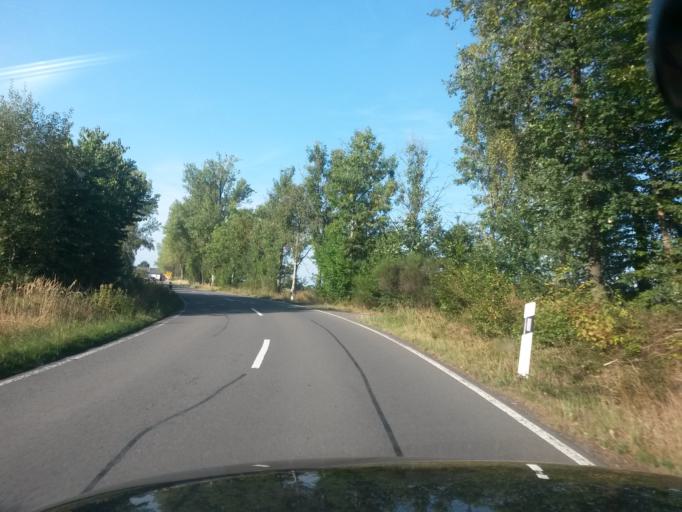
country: DE
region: North Rhine-Westphalia
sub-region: Regierungsbezirk Koln
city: Numbrecht
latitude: 50.8876
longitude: 7.5108
